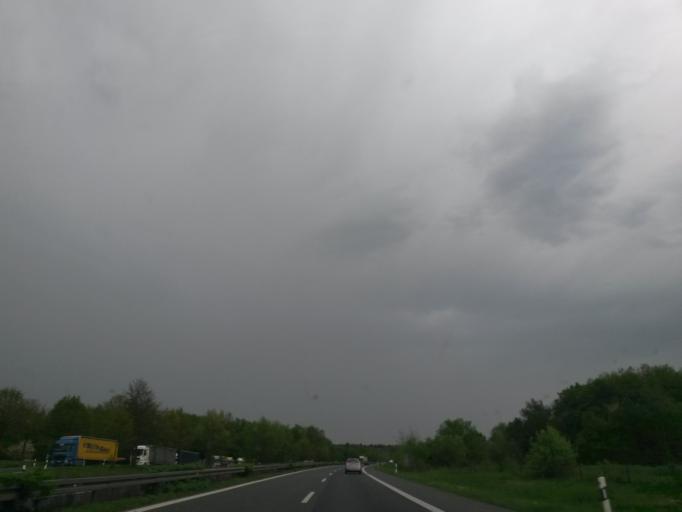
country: DE
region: Bavaria
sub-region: Upper Franconia
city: Eggolsheim
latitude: 49.7573
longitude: 11.0583
